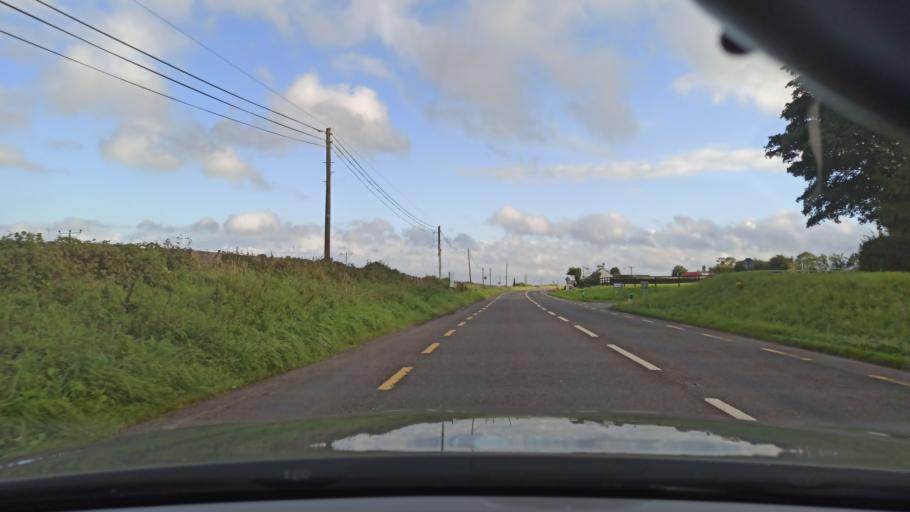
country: IE
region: Munster
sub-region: North Tipperary
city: Roscrea
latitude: 52.9347
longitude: -7.7876
